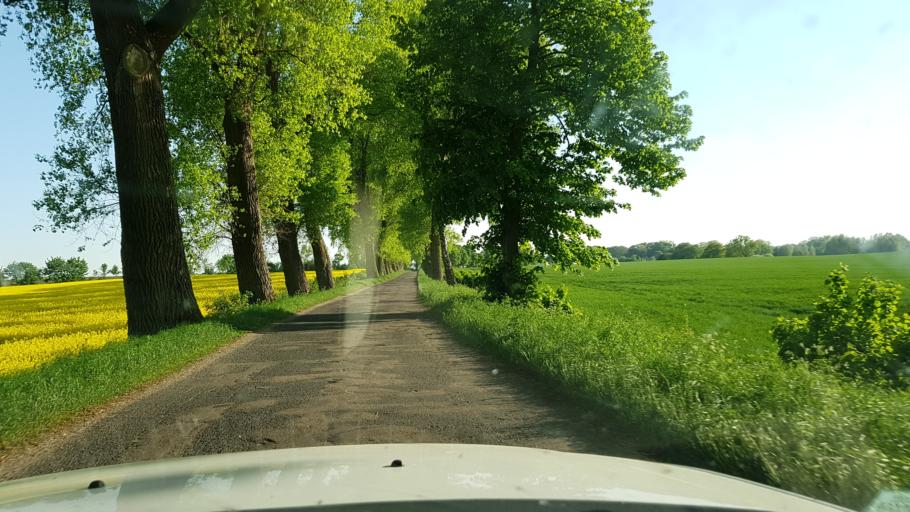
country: PL
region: West Pomeranian Voivodeship
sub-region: Powiat lobeski
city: Dobra
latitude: 53.5888
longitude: 15.3263
